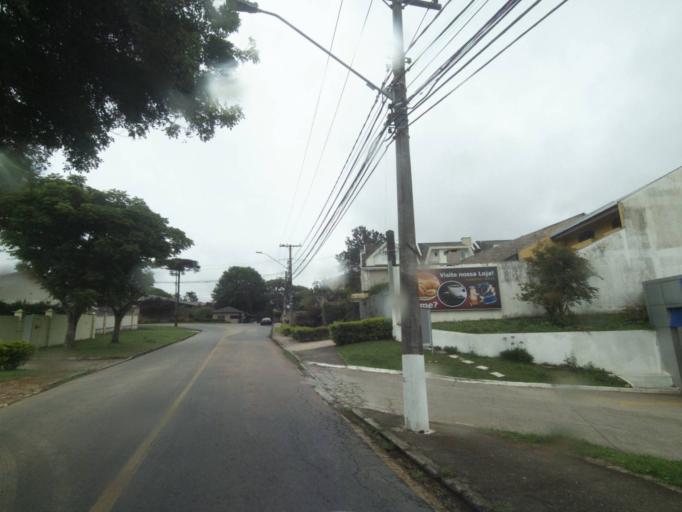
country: BR
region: Parana
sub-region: Curitiba
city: Curitiba
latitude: -25.4210
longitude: -49.3244
